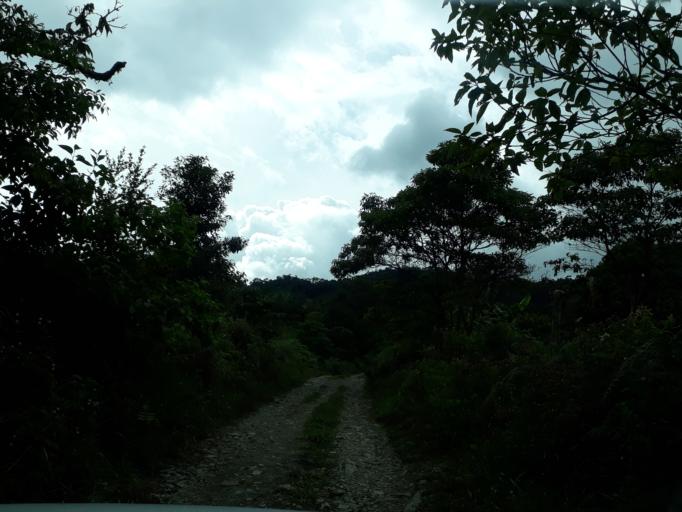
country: CO
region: Boyaca
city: Muzo
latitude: 5.3877
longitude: -74.1041
